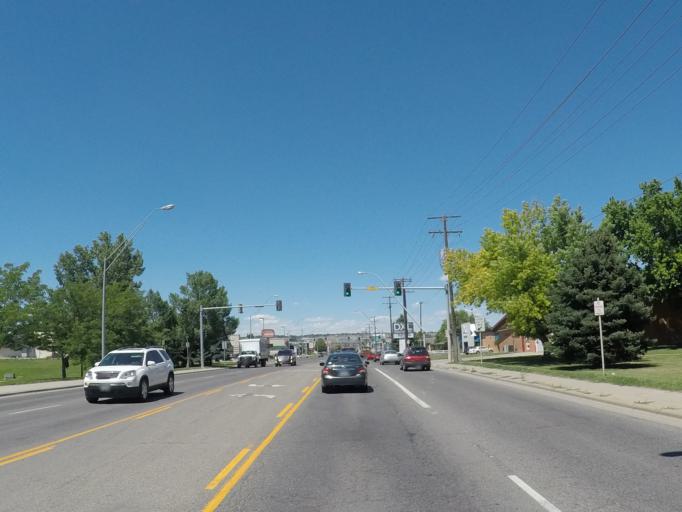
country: US
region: Montana
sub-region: Yellowstone County
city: Billings
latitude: 45.7579
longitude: -108.5762
